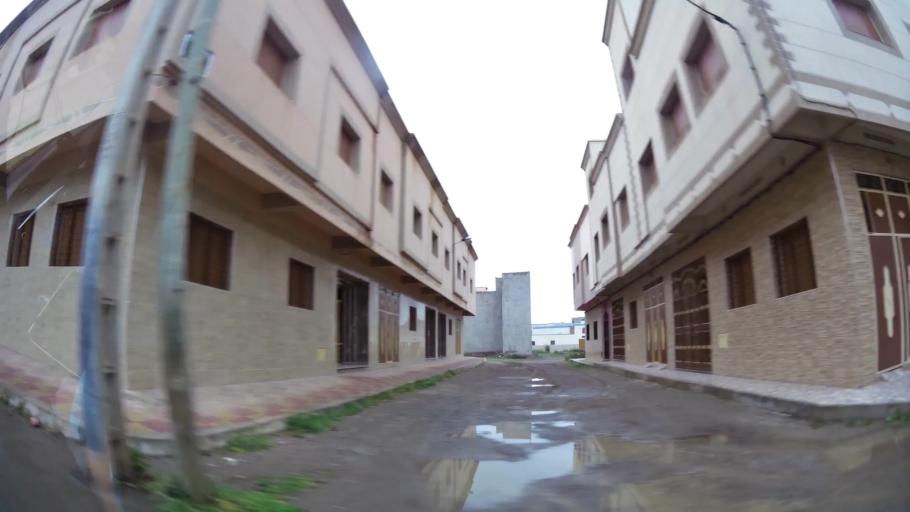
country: MA
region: Oriental
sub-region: Nador
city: Nador
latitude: 35.1631
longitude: -2.9538
